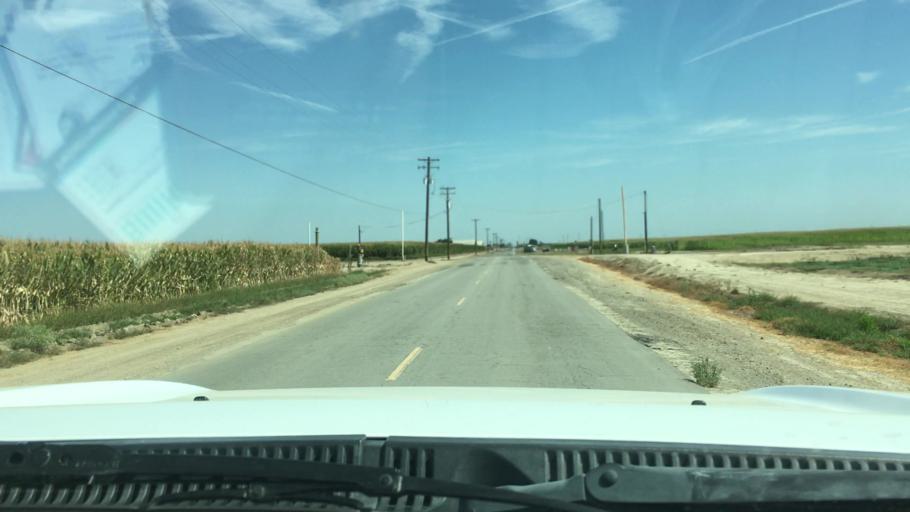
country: US
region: California
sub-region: Kern County
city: Buttonwillow
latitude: 35.4050
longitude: -119.3767
